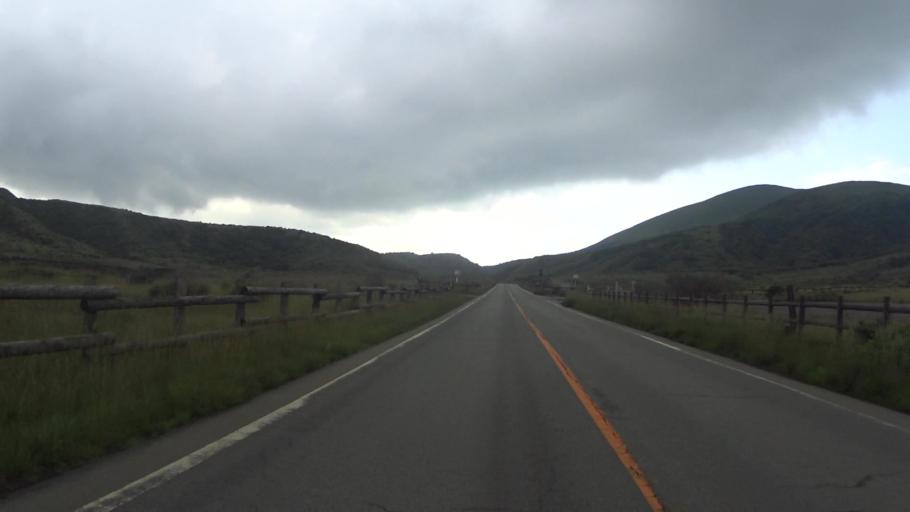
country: JP
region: Kumamoto
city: Aso
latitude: 32.8840
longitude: 131.0649
